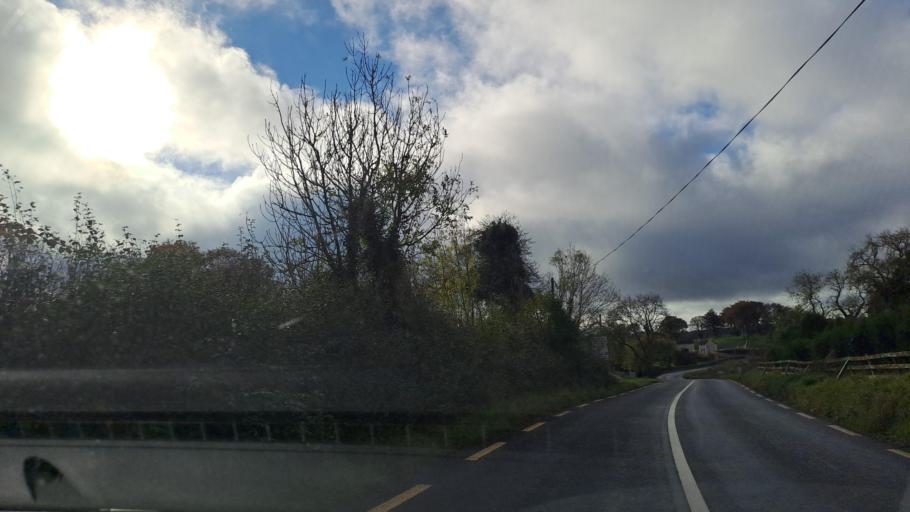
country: IE
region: Ulster
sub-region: An Cabhan
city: Virginia
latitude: 53.8757
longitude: -7.0356
